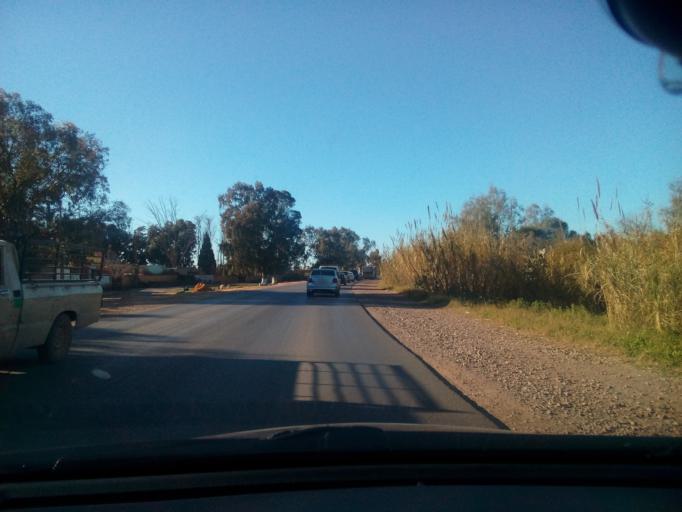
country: DZ
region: Mostaganem
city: Mostaganem
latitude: 35.9015
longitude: 0.2144
